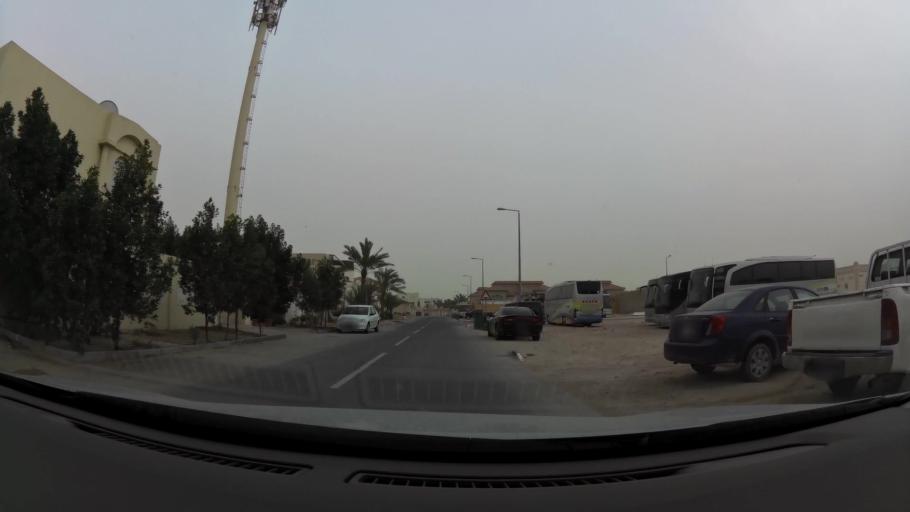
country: QA
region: Baladiyat ad Dawhah
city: Doha
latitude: 25.2506
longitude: 51.4783
